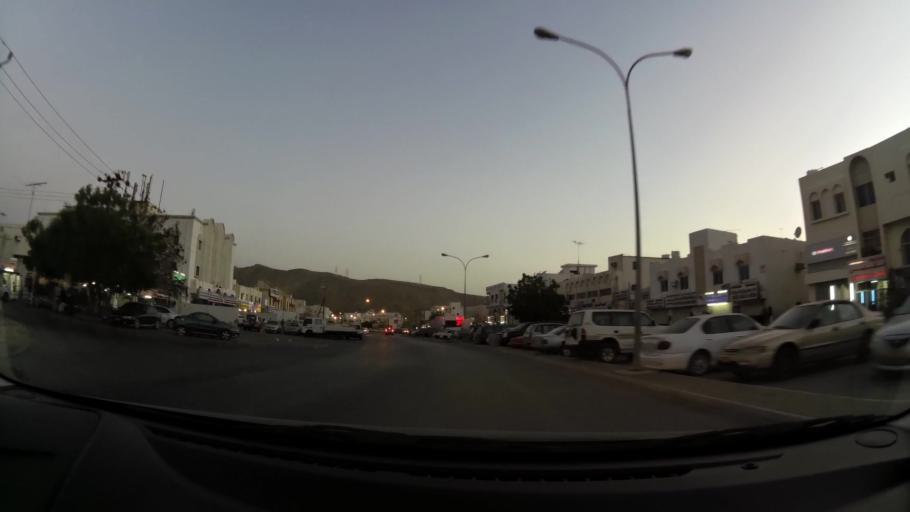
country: OM
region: Muhafazat Masqat
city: Muscat
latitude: 23.5925
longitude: 58.5623
